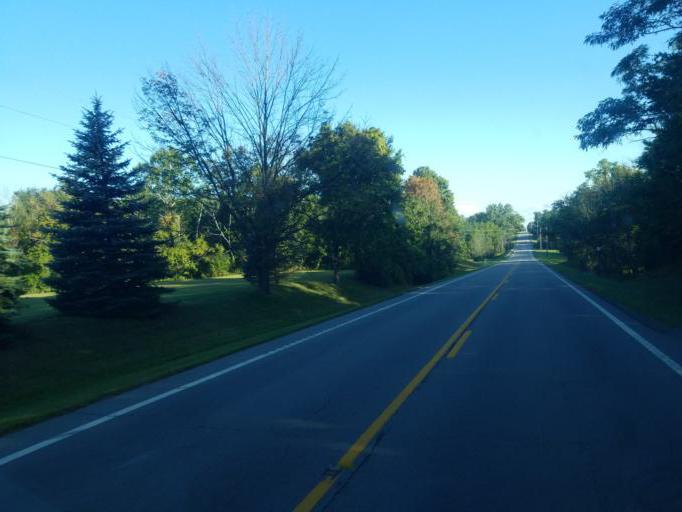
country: US
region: Ohio
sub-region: Lorain County
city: Camden
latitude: 41.1515
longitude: -82.3104
